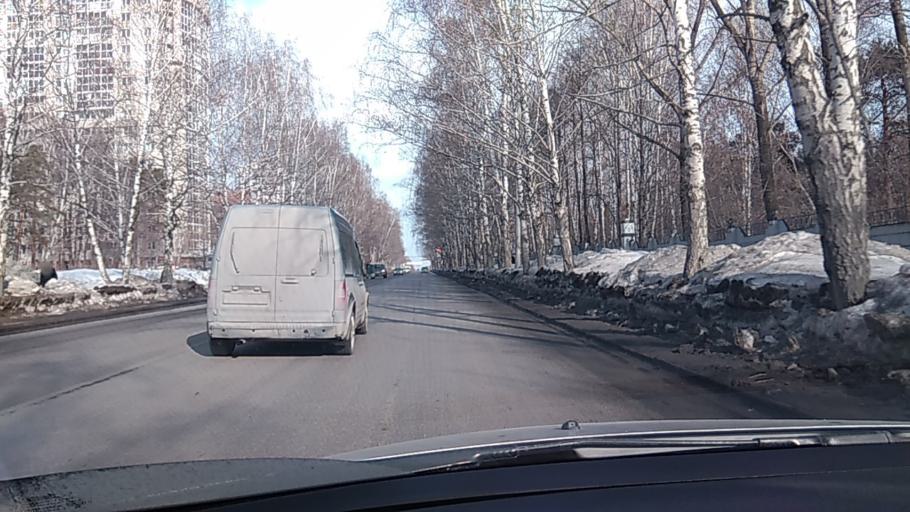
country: RU
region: Sverdlovsk
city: Yekaterinburg
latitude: 56.8489
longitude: 60.6361
